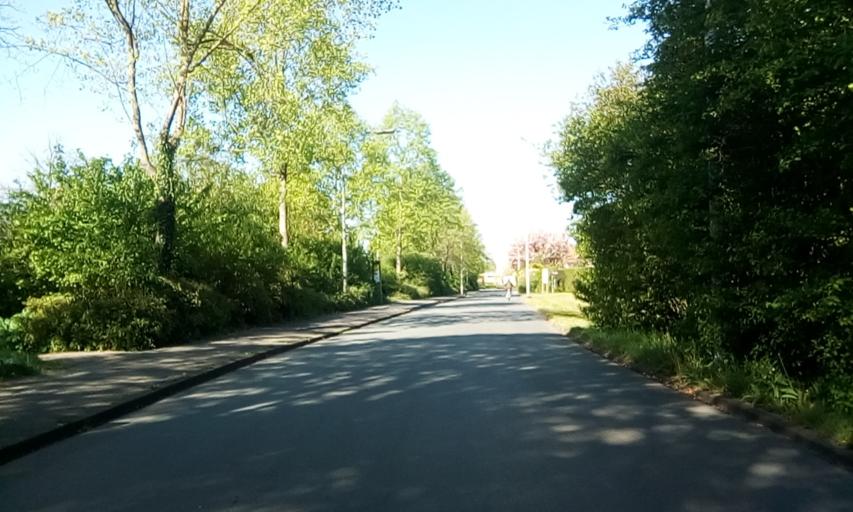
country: NL
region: Gelderland
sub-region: Gemeente Tiel
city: Tiel
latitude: 51.8914
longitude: 5.4173
